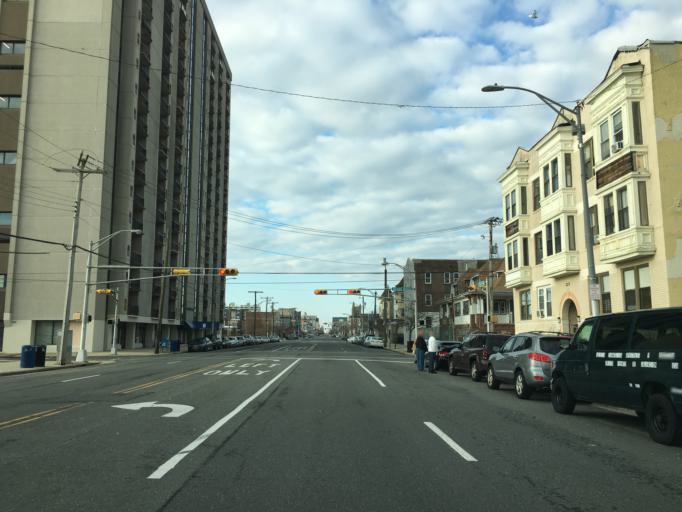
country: US
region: New Jersey
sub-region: Atlantic County
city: Atlantic City
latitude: 39.3680
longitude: -74.4140
